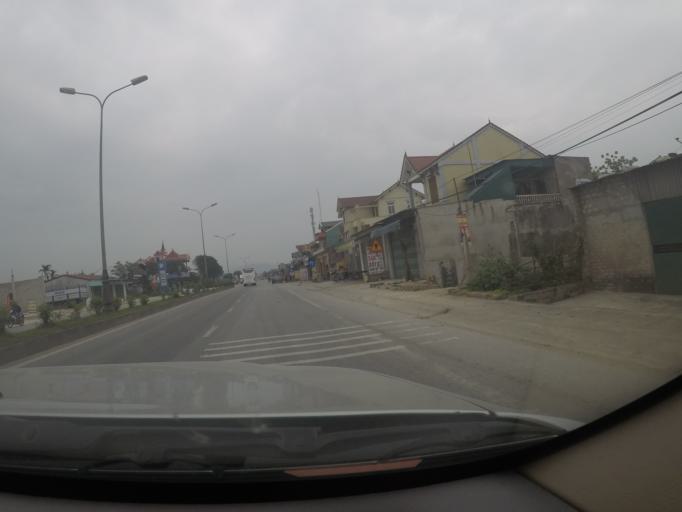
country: VN
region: Nghe An
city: Dien Chau
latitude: 18.9489
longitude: 105.6032
